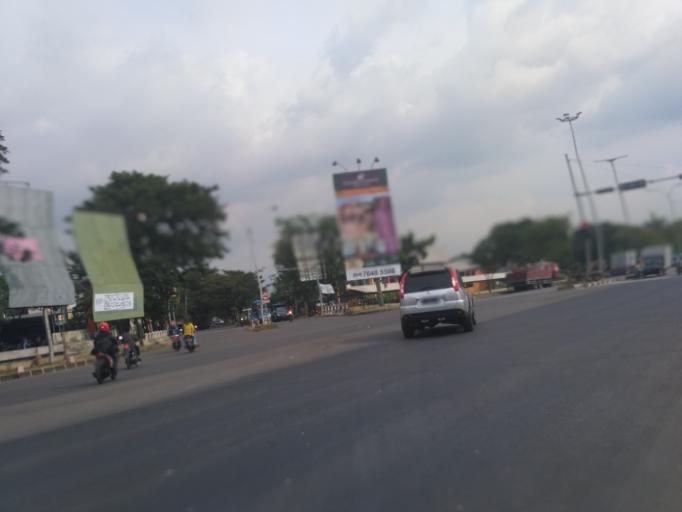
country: ID
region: Central Java
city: Semarang
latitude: -6.9707
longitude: 110.3905
